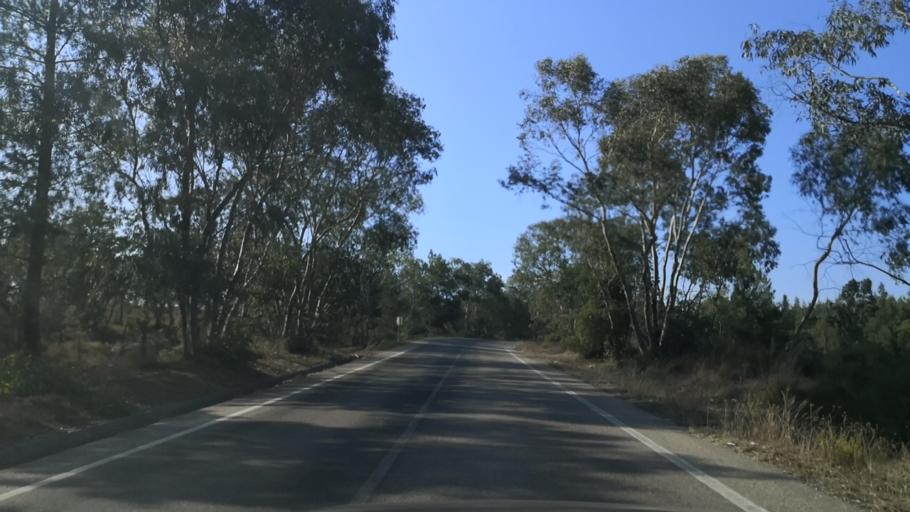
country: PT
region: Santarem
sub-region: Almeirim
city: Fazendas de Almeirim
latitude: 39.0953
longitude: -8.5750
